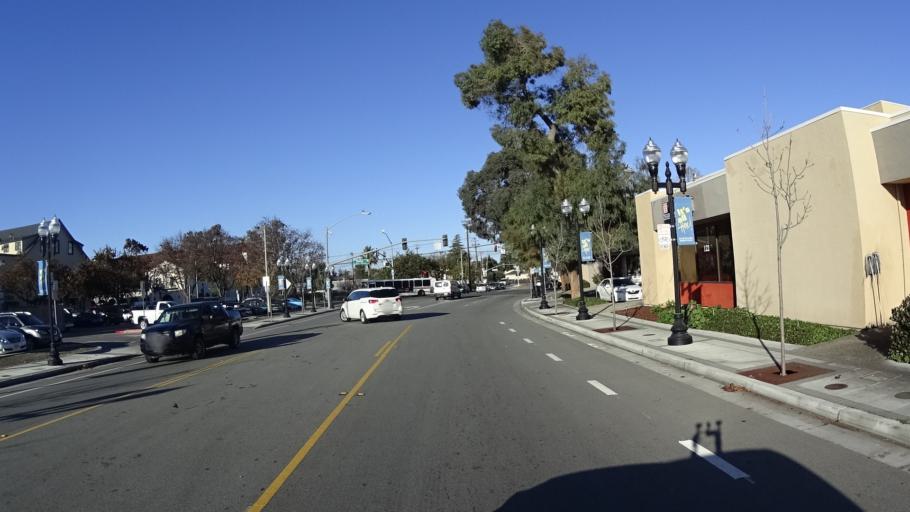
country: US
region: California
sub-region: Santa Clara County
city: Sunnyvale
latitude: 37.3764
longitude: -122.0290
